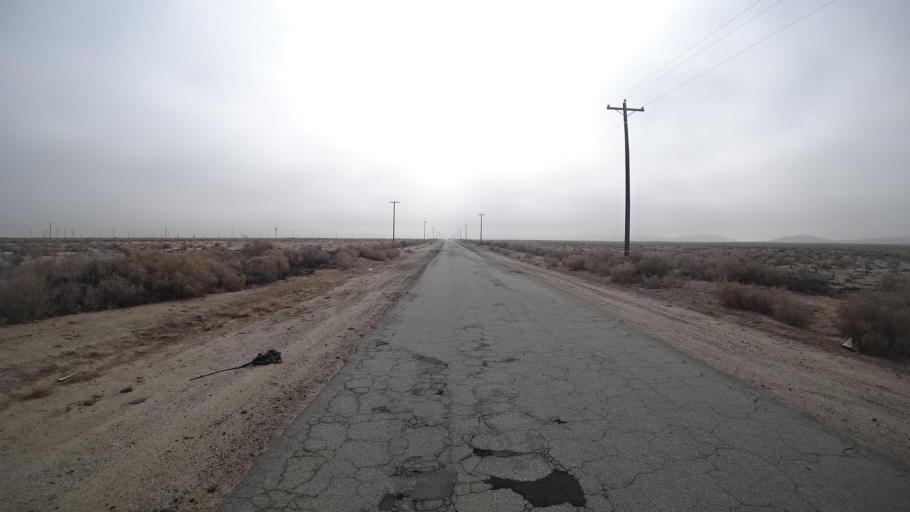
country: US
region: California
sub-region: Kern County
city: Ford City
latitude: 35.2043
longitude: -119.4290
